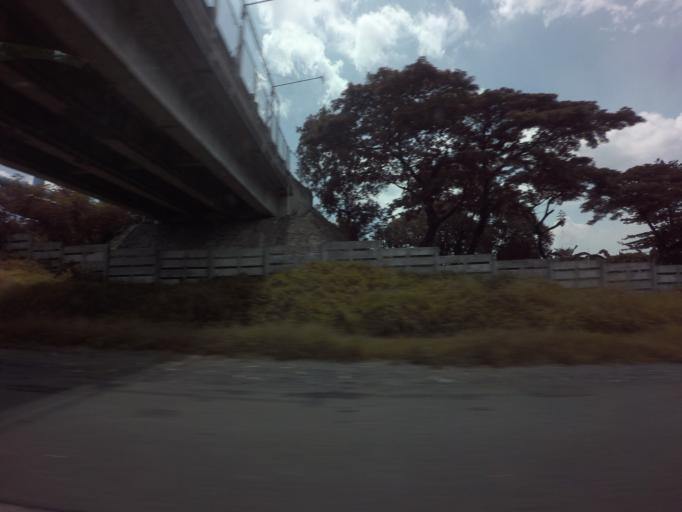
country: PH
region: Calabarzon
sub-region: Province of Laguna
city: San Pedro
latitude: 14.3772
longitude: 121.0232
